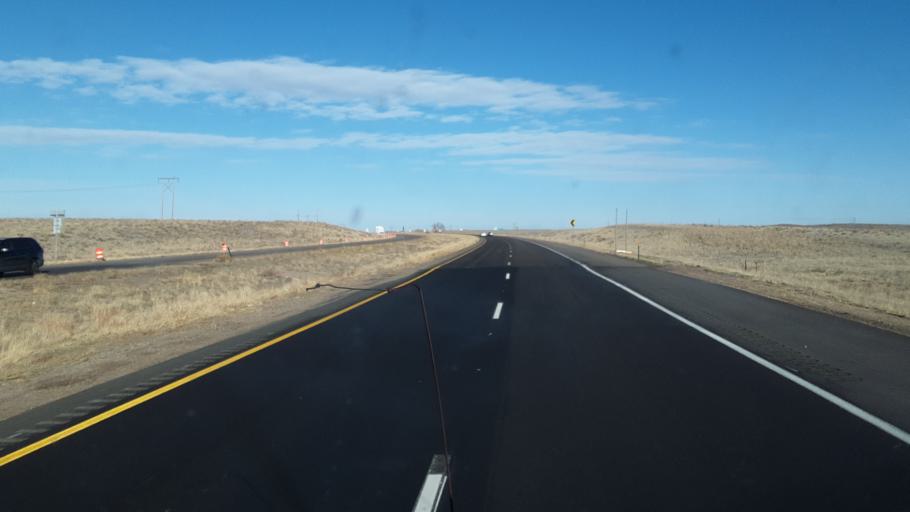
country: US
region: Colorado
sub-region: Morgan County
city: Brush
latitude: 40.2746
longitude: -103.5743
